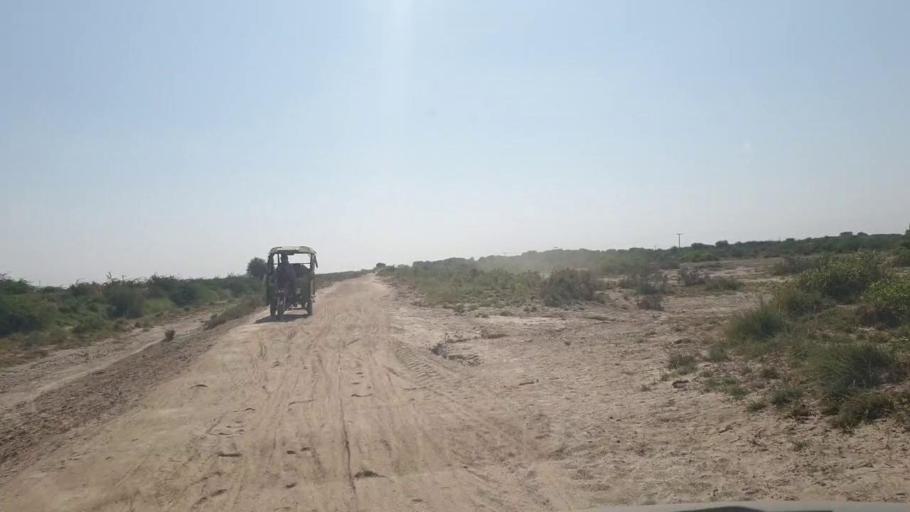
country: PK
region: Sindh
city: Tando Bago
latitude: 24.9212
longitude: 69.1645
